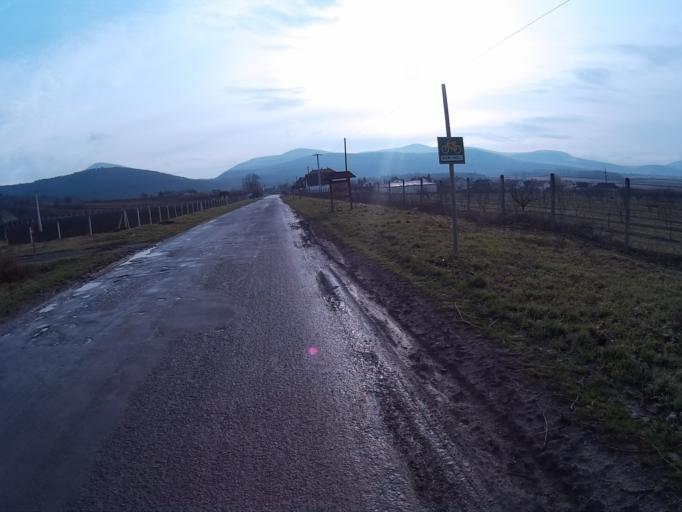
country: HU
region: Borsod-Abauj-Zemplen
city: Abaujszanto
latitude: 48.3408
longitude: 21.2253
